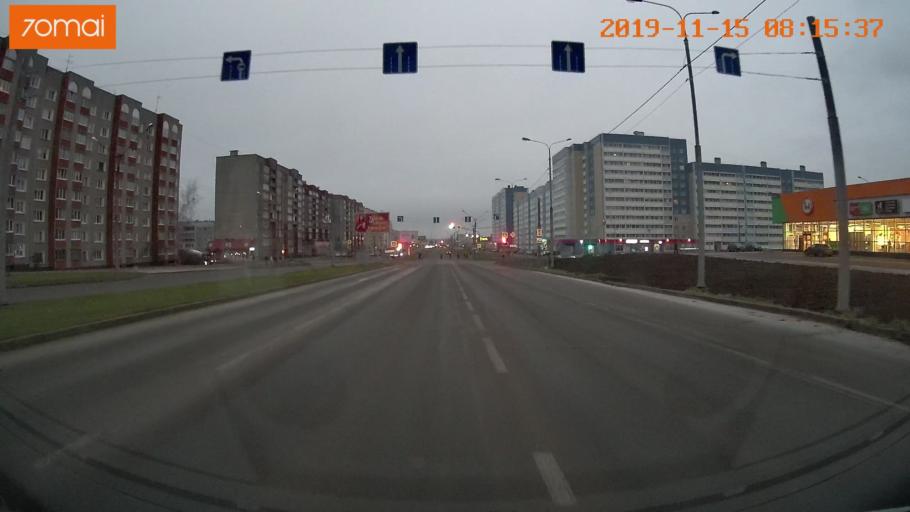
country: RU
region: Vologda
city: Cherepovets
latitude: 59.0838
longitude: 37.9213
